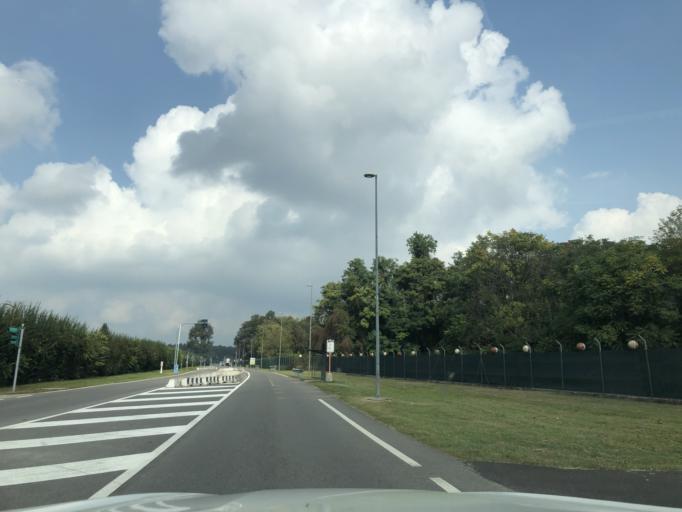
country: IT
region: Lombardy
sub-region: Provincia di Varese
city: Vizzola Ticino
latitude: 45.6420
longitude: 8.7128
